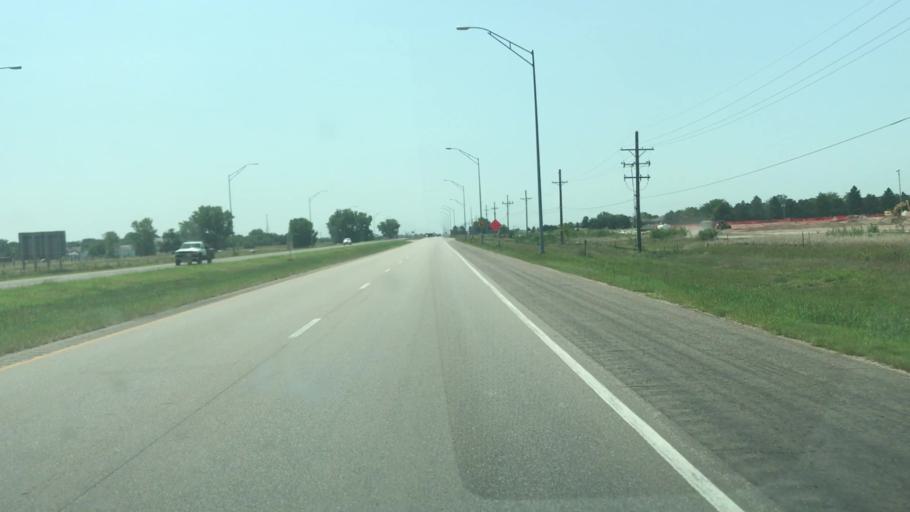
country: US
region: Nebraska
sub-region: Hall County
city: Grand Island
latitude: 40.8834
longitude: -98.3783
